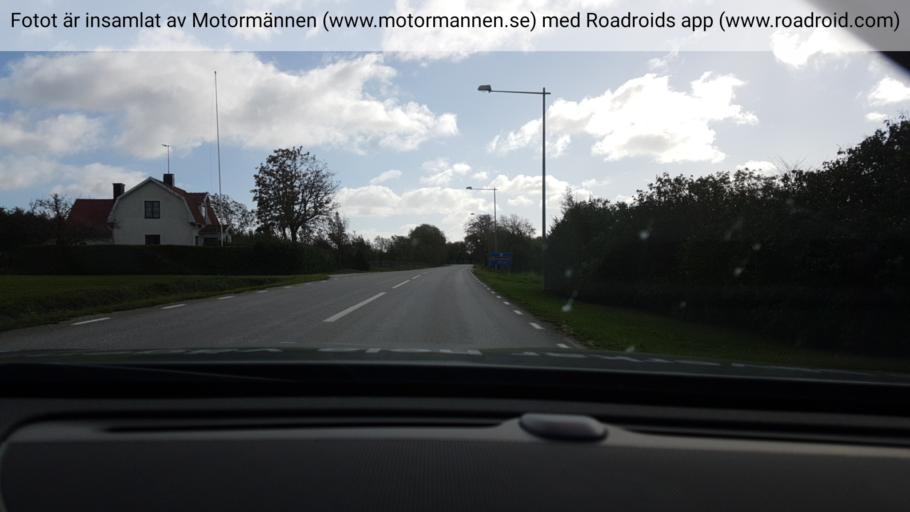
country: SE
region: Gotland
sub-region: Gotland
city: Slite
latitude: 57.8559
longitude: 19.0183
